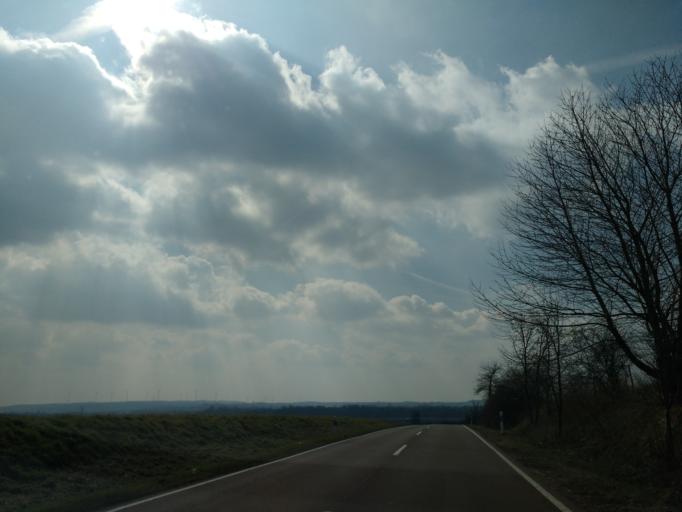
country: DE
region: Saxony-Anhalt
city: Roblingen am See
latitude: 51.4835
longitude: 11.6744
